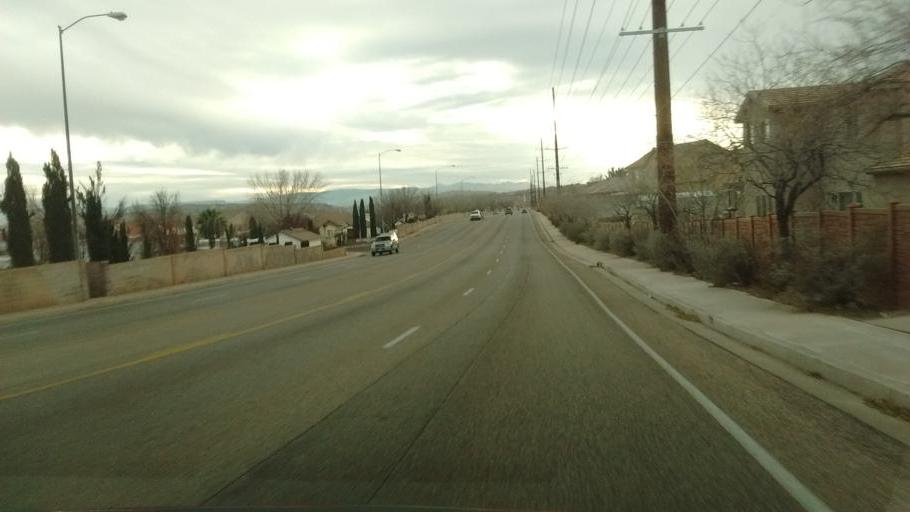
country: US
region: Utah
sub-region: Washington County
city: Washington
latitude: 37.1105
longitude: -113.5219
